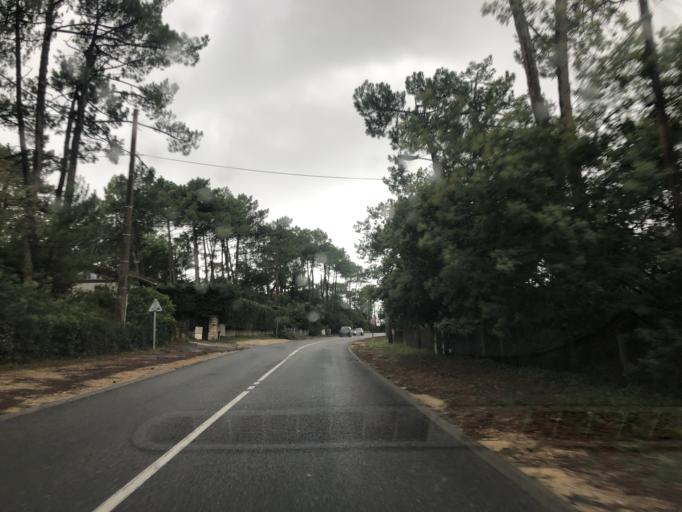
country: FR
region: Aquitaine
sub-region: Departement de la Gironde
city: Arcachon
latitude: 44.6958
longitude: -1.2330
